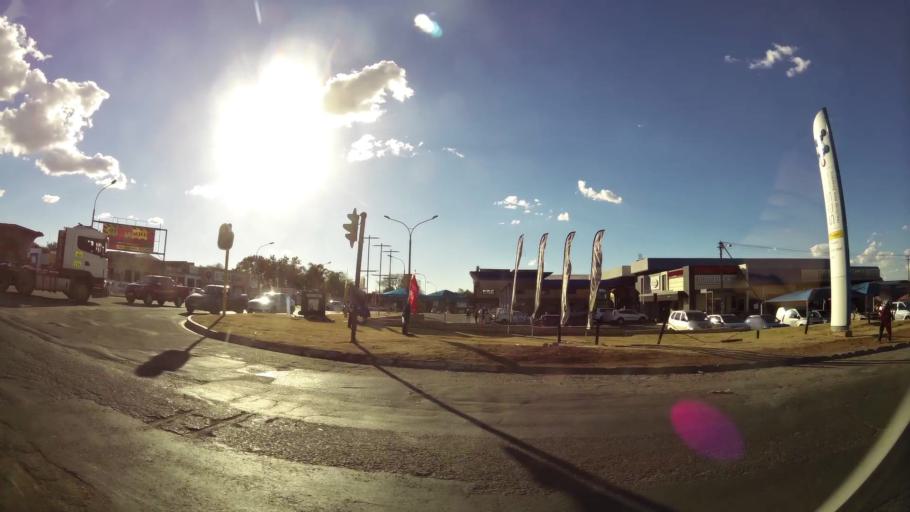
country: ZA
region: North-West
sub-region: Dr Kenneth Kaunda District Municipality
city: Klerksdorp
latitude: -26.8507
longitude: 26.6906
